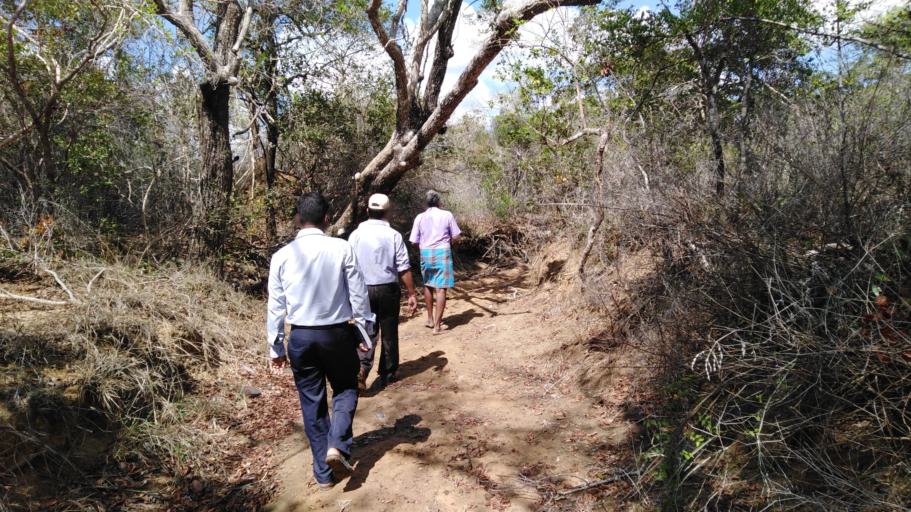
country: LK
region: Northern Province
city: Kilinochchi
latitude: 9.2824
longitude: 80.2864
